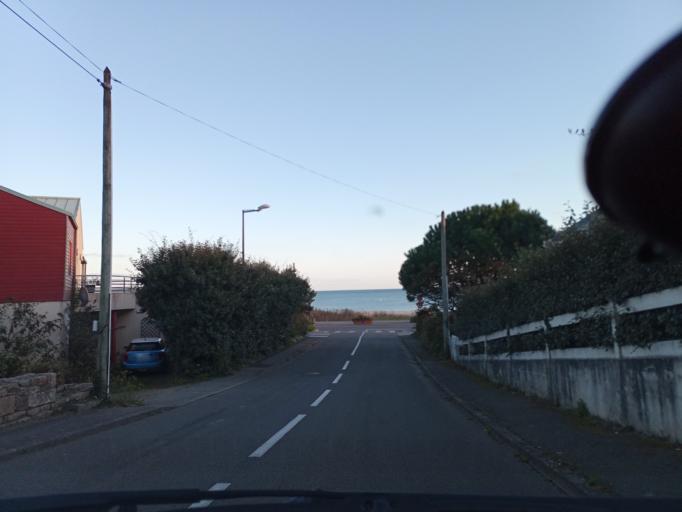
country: FR
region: Brittany
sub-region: Departement du Finistere
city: Audierne
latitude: 48.0126
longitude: -4.5501
